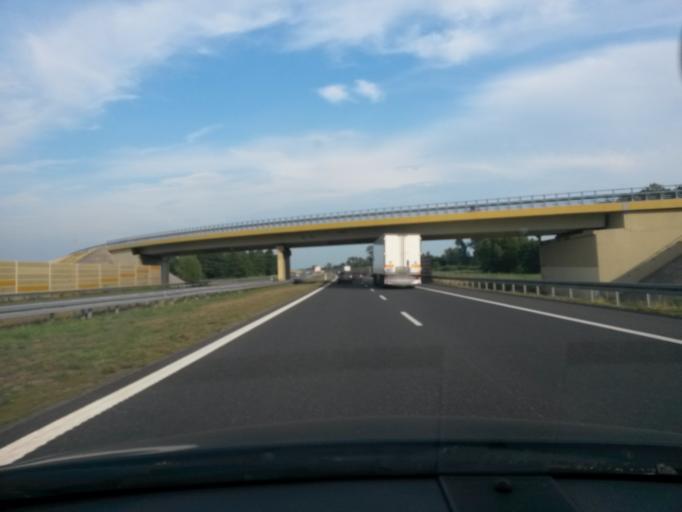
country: PL
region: Lodz Voivodeship
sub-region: Powiat poddebicki
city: Wartkowice
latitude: 51.9736
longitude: 19.0853
